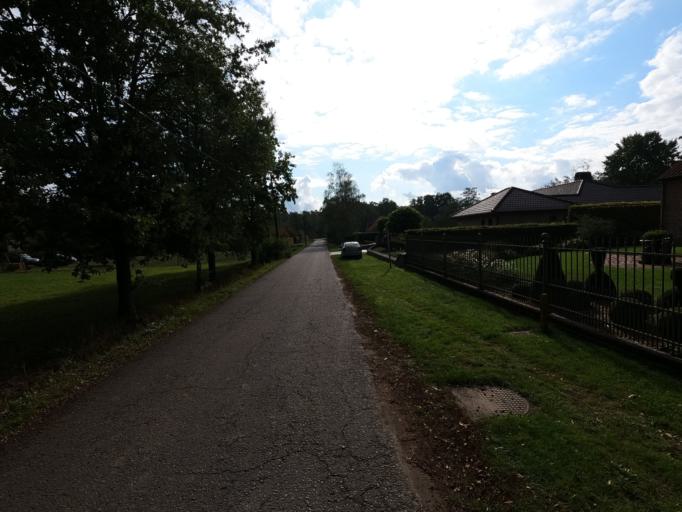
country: BE
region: Flanders
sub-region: Provincie Antwerpen
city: Kasterlee
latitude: 51.2110
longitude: 4.9095
